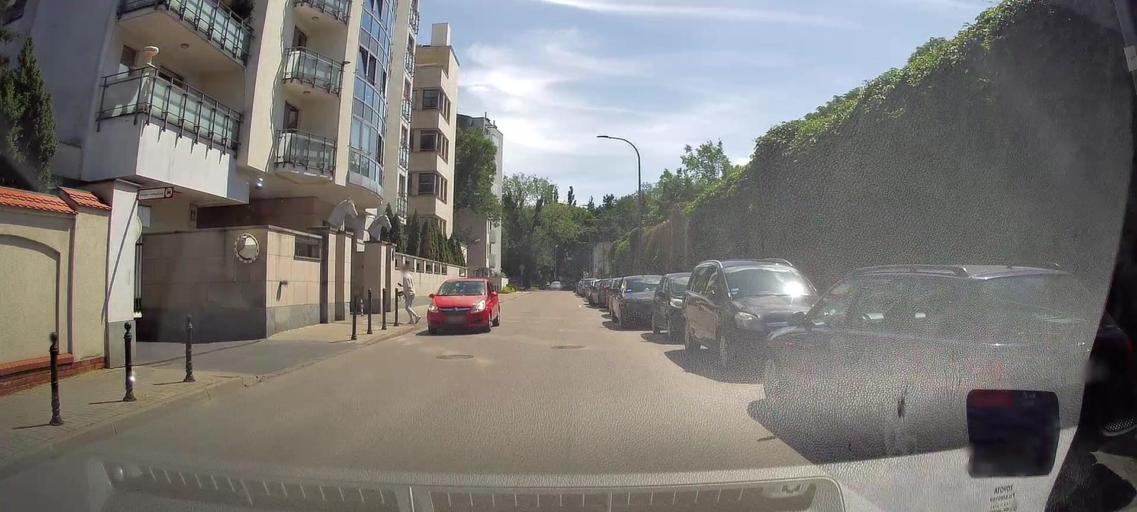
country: PL
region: Masovian Voivodeship
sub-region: Warszawa
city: Mokotow
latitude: 52.1665
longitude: 21.0120
